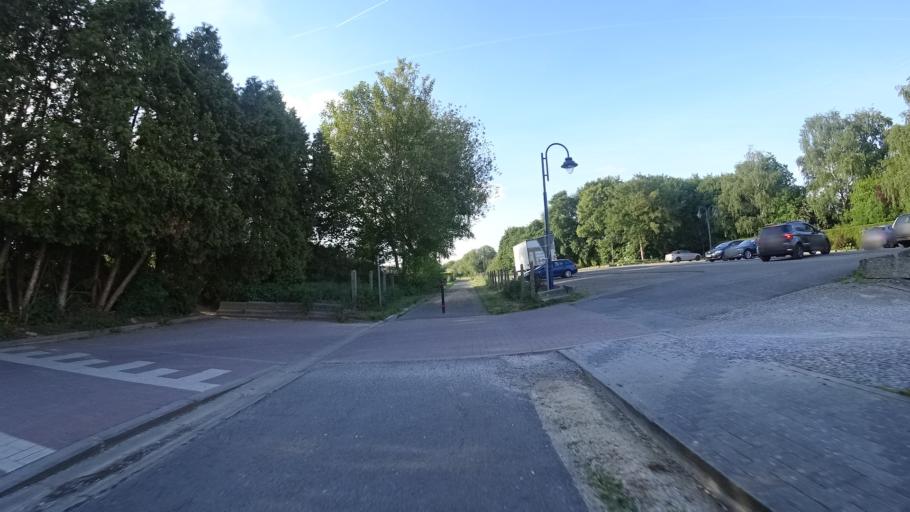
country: BE
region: Wallonia
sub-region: Province de Namur
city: Eghezee
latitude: 50.5970
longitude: 4.9102
